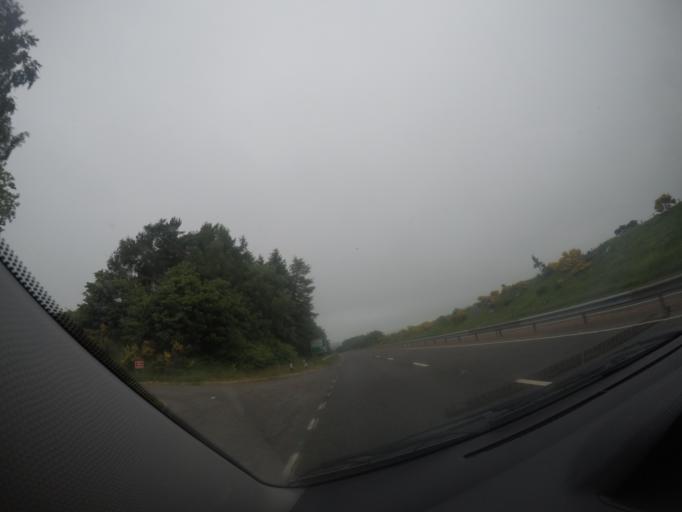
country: GB
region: Scotland
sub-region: Angus
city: Forfar
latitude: 56.5793
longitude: -2.9133
